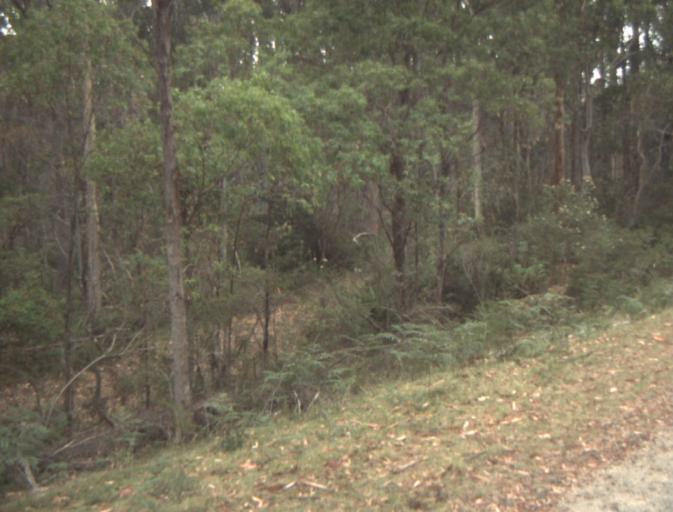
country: AU
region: Tasmania
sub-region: Dorset
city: Scottsdale
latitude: -41.4000
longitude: 147.5172
